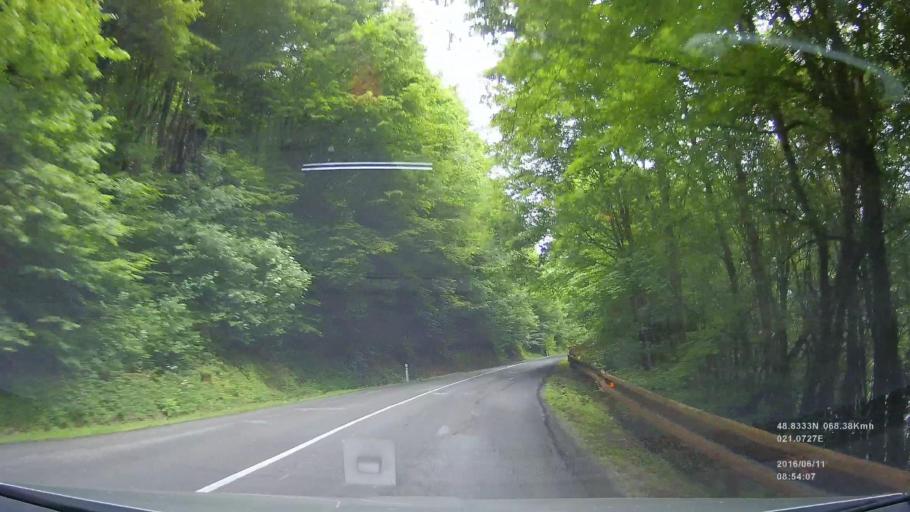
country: SK
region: Kosicky
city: Gelnica
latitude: 48.8303
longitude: 21.0772
